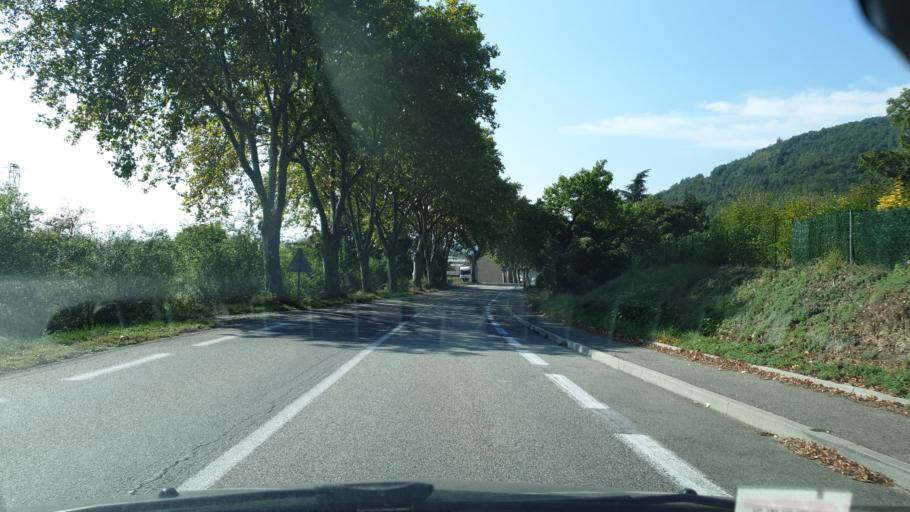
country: FR
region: Rhone-Alpes
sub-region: Departement de l'Ardeche
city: Beauchastel
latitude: 44.8343
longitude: 4.8121
